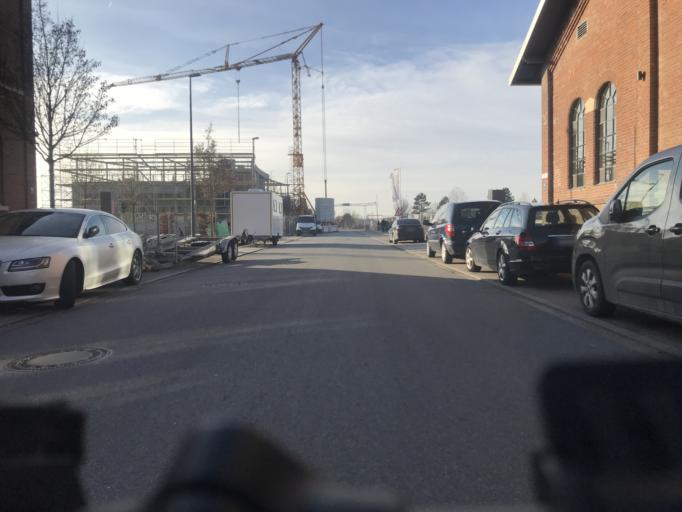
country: DE
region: Bavaria
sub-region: Upper Bavaria
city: Grafelfing
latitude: 48.1362
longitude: 11.4200
